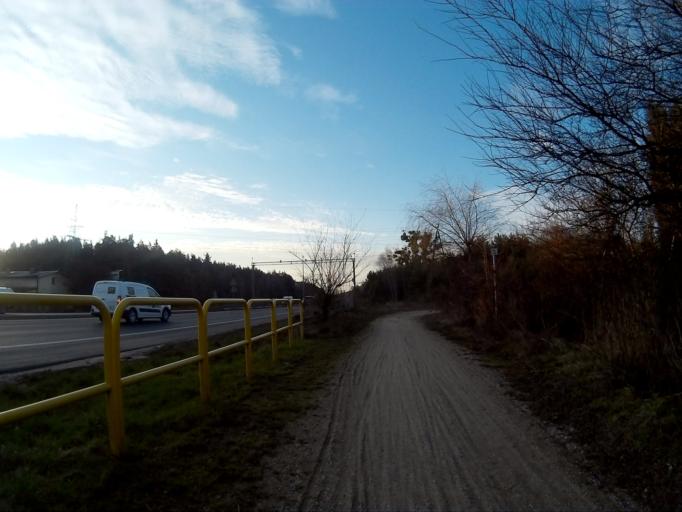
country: PL
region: Kujawsko-Pomorskie
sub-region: Powiat bydgoski
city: Osielsko
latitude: 53.1609
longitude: 18.0539
